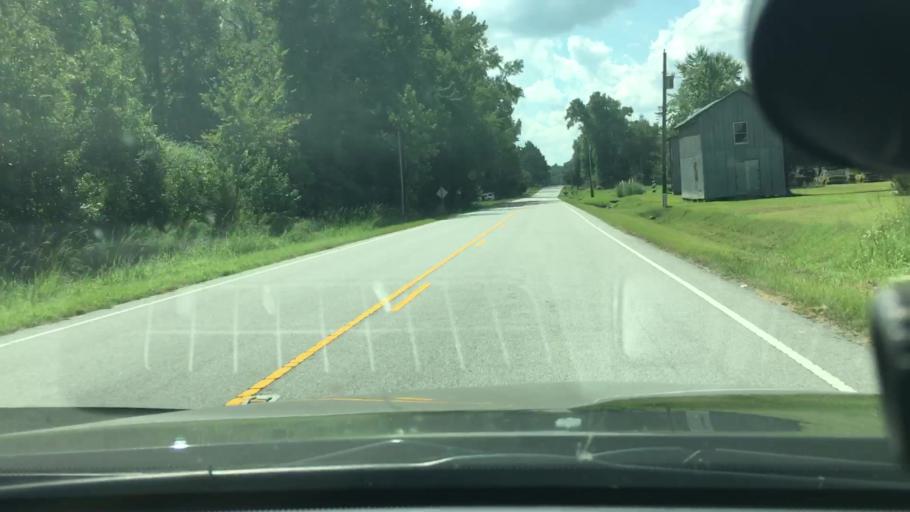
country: US
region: North Carolina
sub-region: Edgecombe County
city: Pinetops
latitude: 35.7316
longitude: -77.5326
